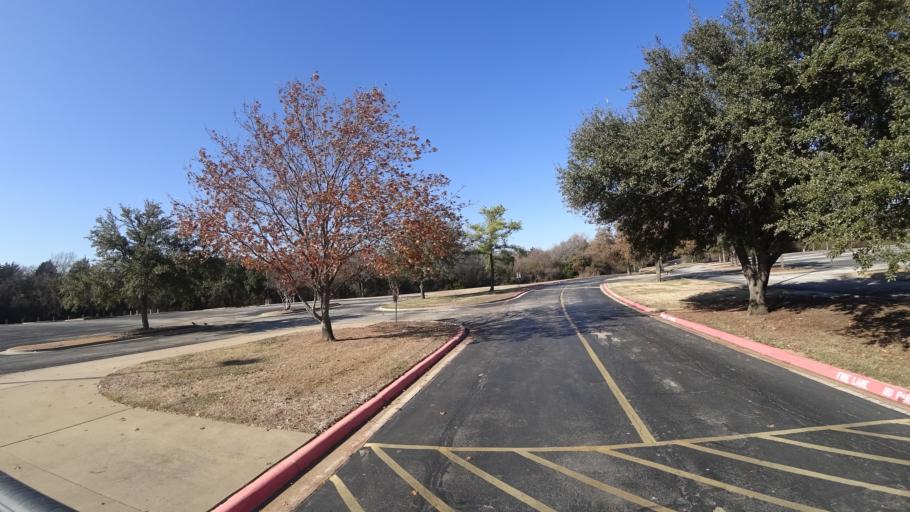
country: US
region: Texas
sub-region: Dallas County
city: Coppell
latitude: 32.9970
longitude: -97.0039
